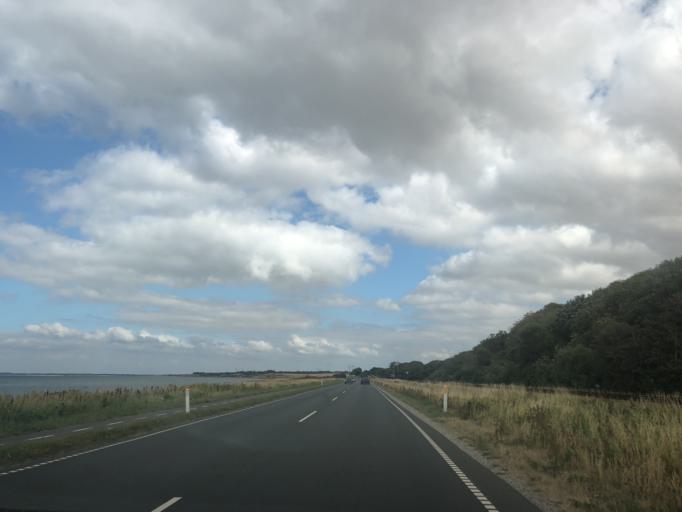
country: DK
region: Central Jutland
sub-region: Struer Kommune
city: Struer
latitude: 56.4669
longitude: 8.6478
